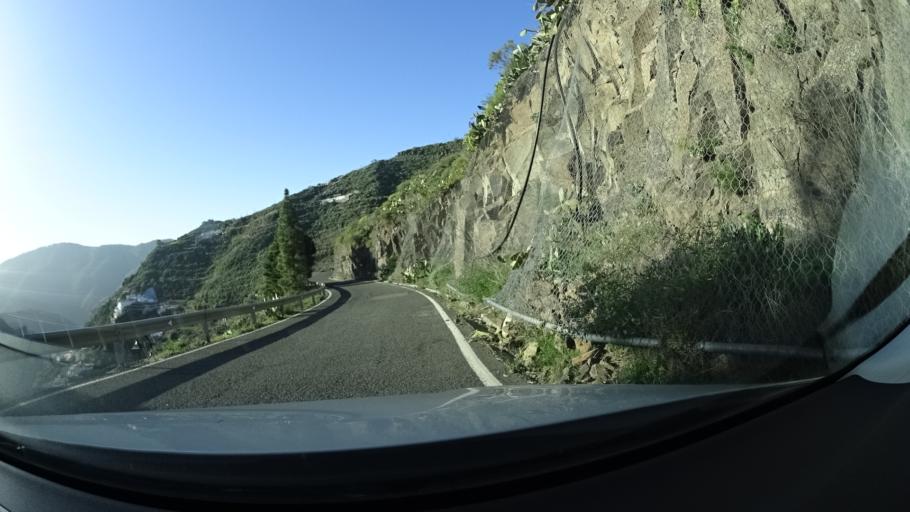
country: ES
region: Canary Islands
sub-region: Provincia de Las Palmas
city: Artenara
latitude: 28.0422
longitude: -15.6473
